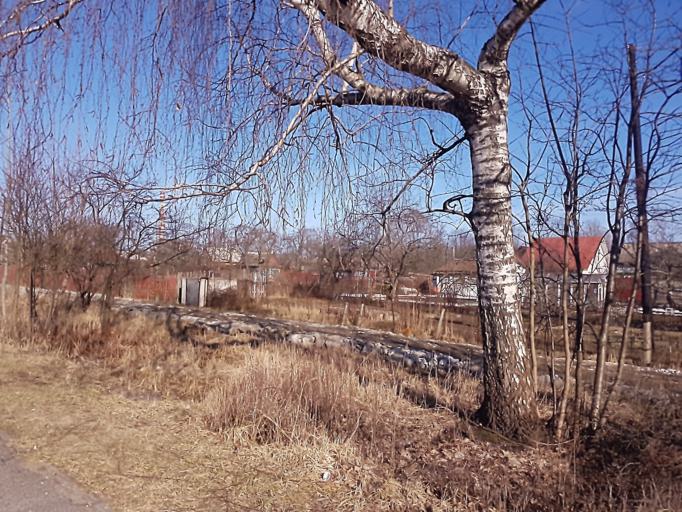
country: BY
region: Mogilev
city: Babruysk
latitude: 53.1848
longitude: 29.2214
